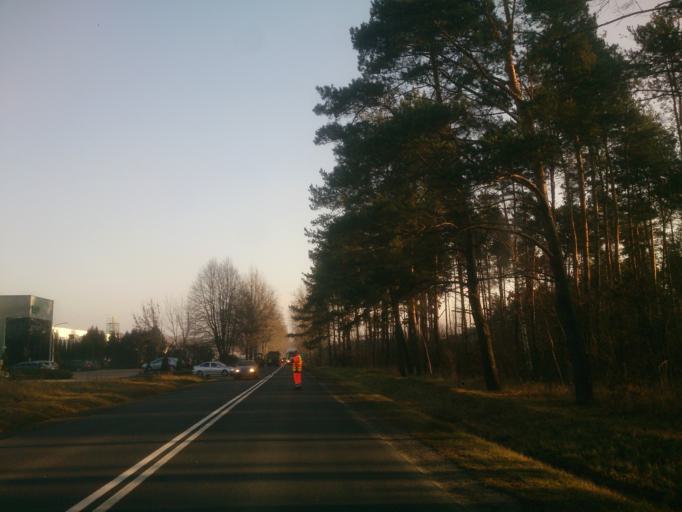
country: PL
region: Kujawsko-Pomorskie
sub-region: Powiat brodnicki
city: Brodnica
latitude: 53.2741
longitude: 19.4281
